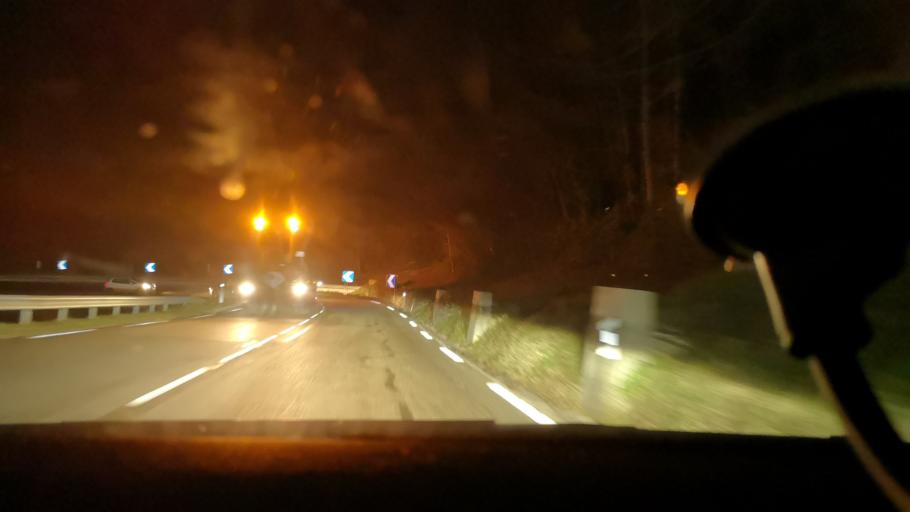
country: FR
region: Franche-Comte
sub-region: Departement du Jura
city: Poligny
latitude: 46.8272
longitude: 5.7262
